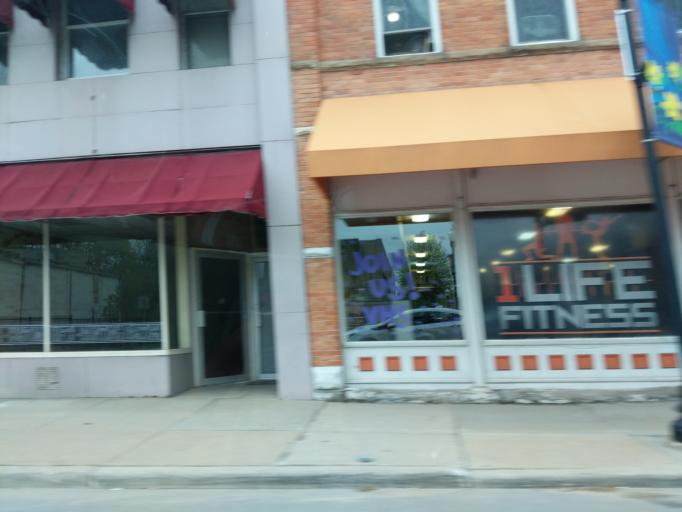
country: US
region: Michigan
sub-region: Tuscola County
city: Vassar
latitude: 43.3716
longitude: -83.5822
